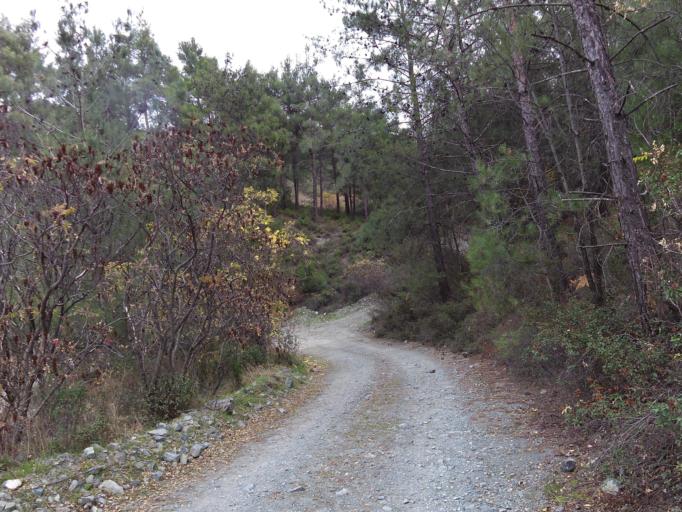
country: CY
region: Limassol
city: Kyperounta
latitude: 34.9243
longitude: 32.9455
